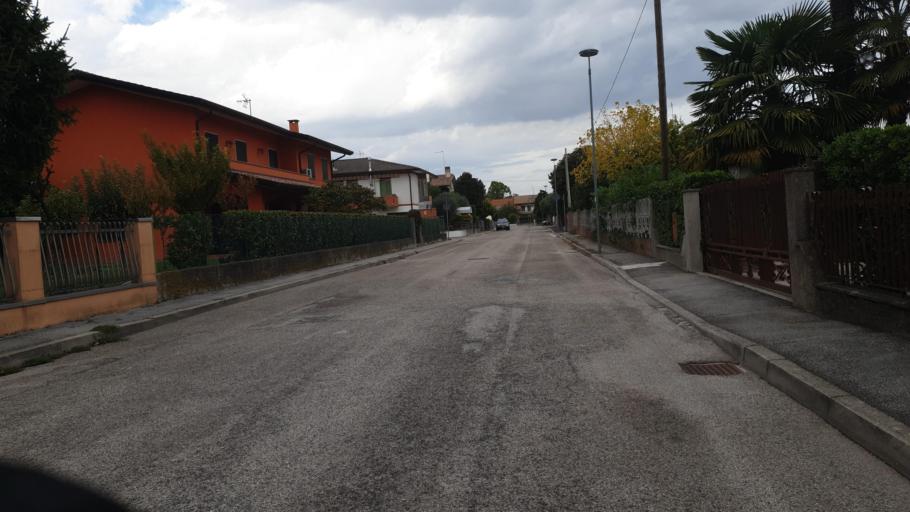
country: IT
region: Veneto
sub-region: Provincia di Padova
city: Casalserugo
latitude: 45.3189
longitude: 11.9146
